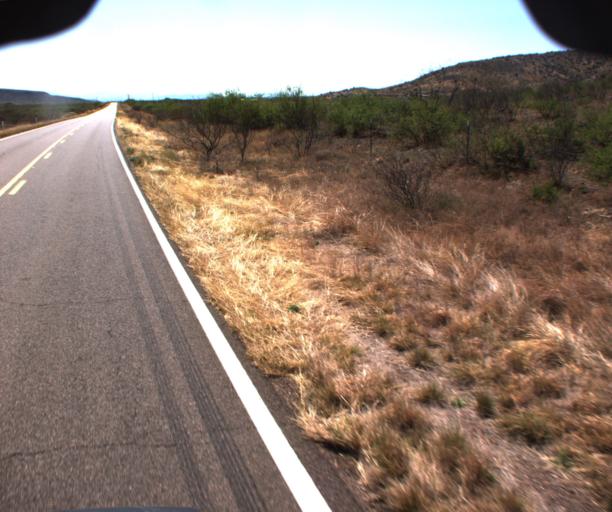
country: US
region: Arizona
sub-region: Cochise County
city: Douglas
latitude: 31.4902
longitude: -109.4230
